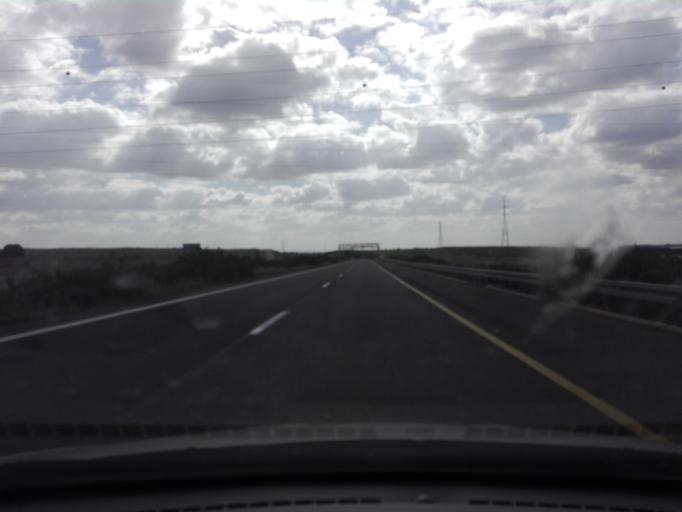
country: PS
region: West Bank
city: Barta`ah ash Sharqiyah
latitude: 32.4982
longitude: 35.0265
